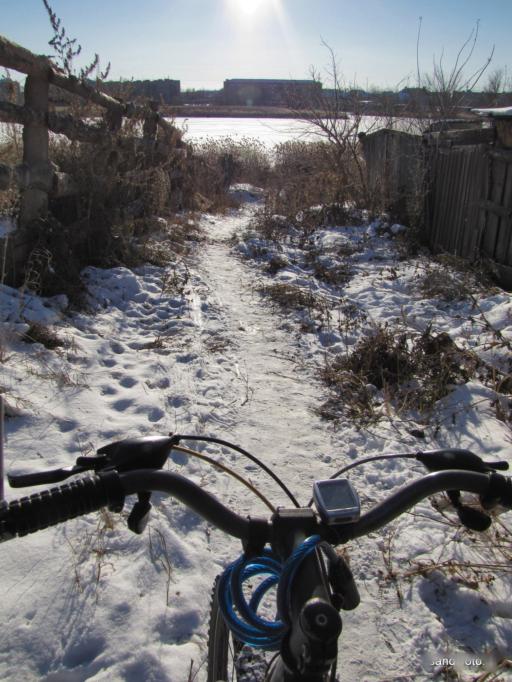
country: RU
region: Chelyabinsk
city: Troitsk
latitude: 54.0954
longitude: 61.5605
